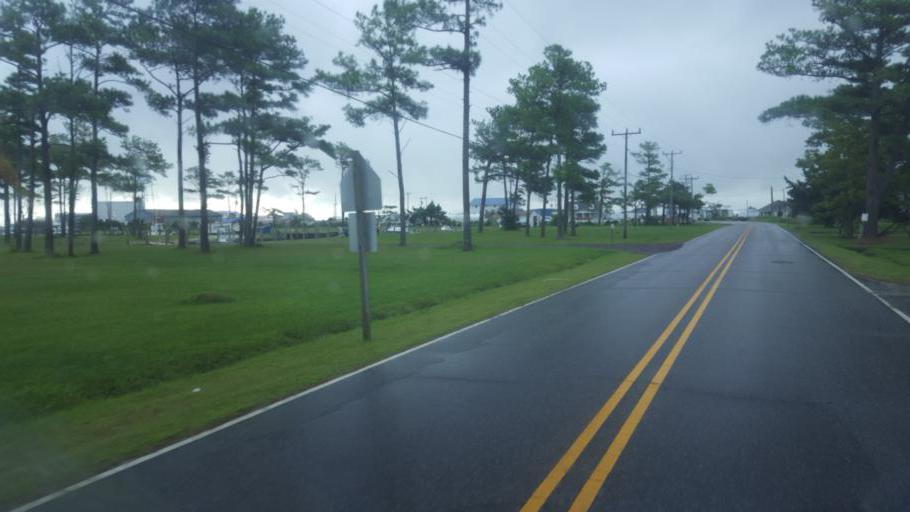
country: US
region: North Carolina
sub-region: Dare County
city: Wanchese
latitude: 35.8425
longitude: -75.6249
